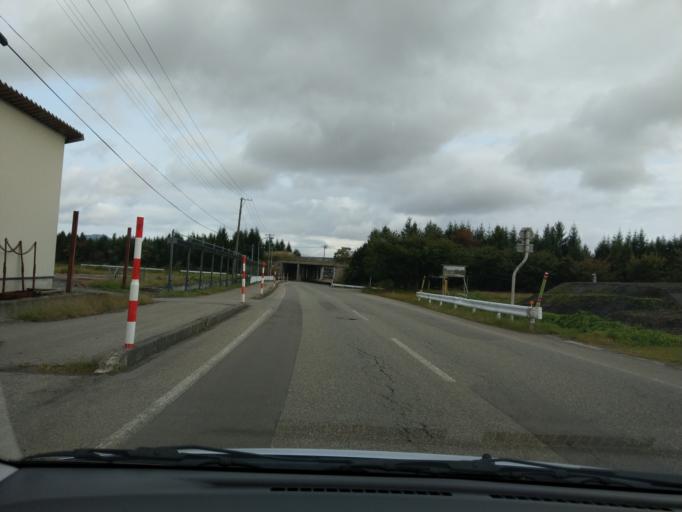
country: JP
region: Akita
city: Omagari
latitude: 39.3977
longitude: 140.4737
